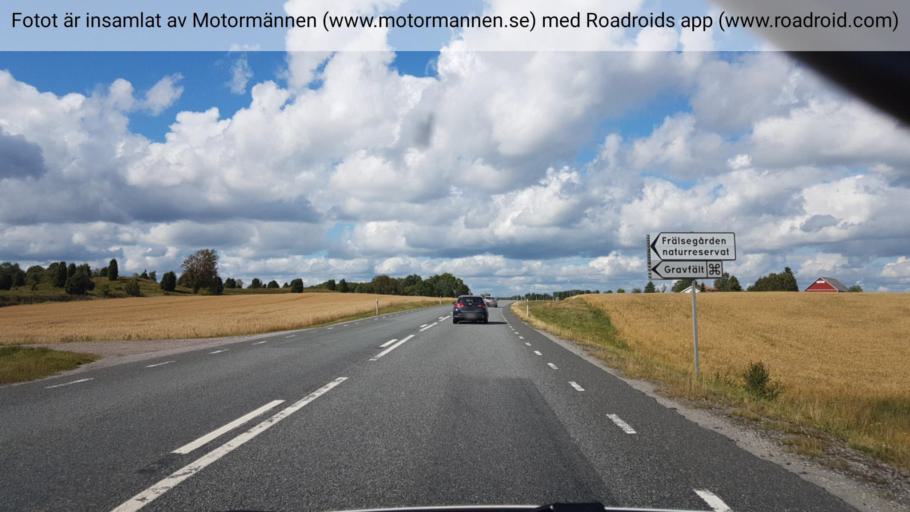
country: SE
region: Vaestra Goetaland
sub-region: Falkopings Kommun
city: Falkoeping
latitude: 57.9763
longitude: 13.5282
